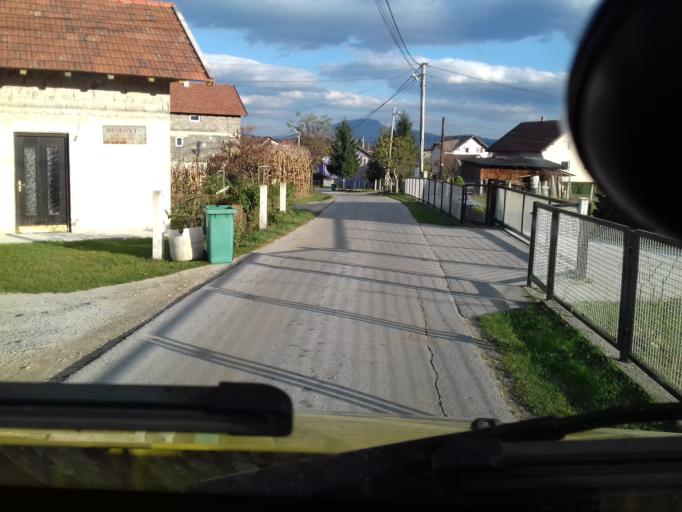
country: BA
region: Federation of Bosnia and Herzegovina
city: Vitez
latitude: 44.1549
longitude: 17.8059
